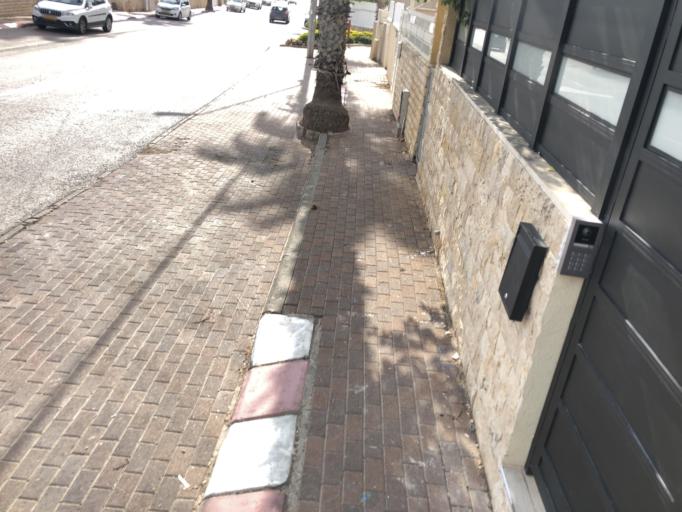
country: IL
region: Northern District
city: `Akko
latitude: 32.9343
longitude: 35.0932
